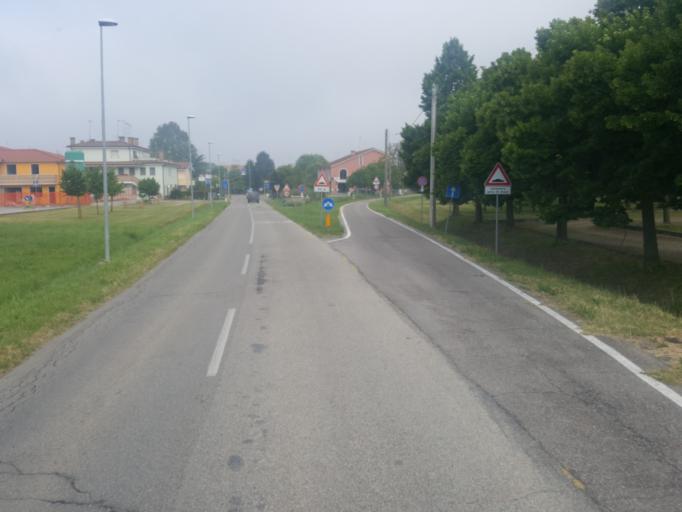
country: IT
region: Veneto
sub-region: Provincia di Rovigo
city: Canaro
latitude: 44.9314
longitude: 11.6785
